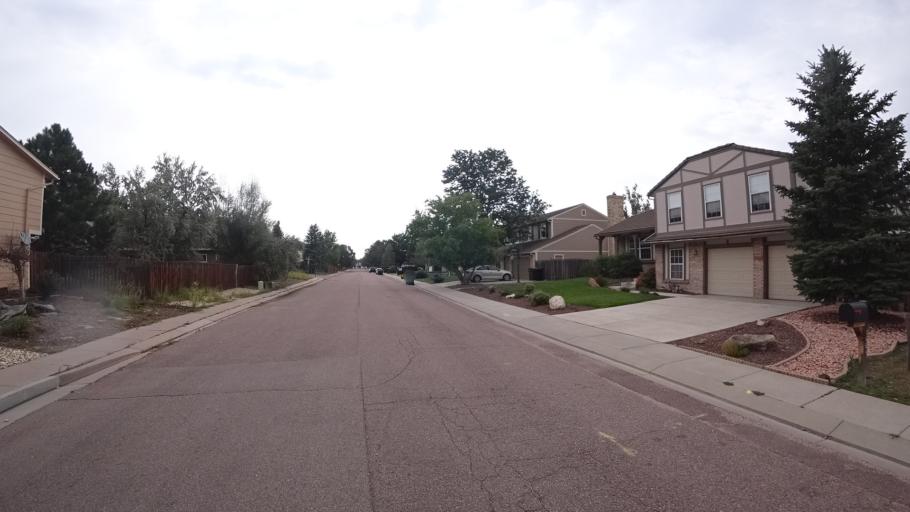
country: US
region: Colorado
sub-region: El Paso County
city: Air Force Academy
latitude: 38.9228
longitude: -104.8362
